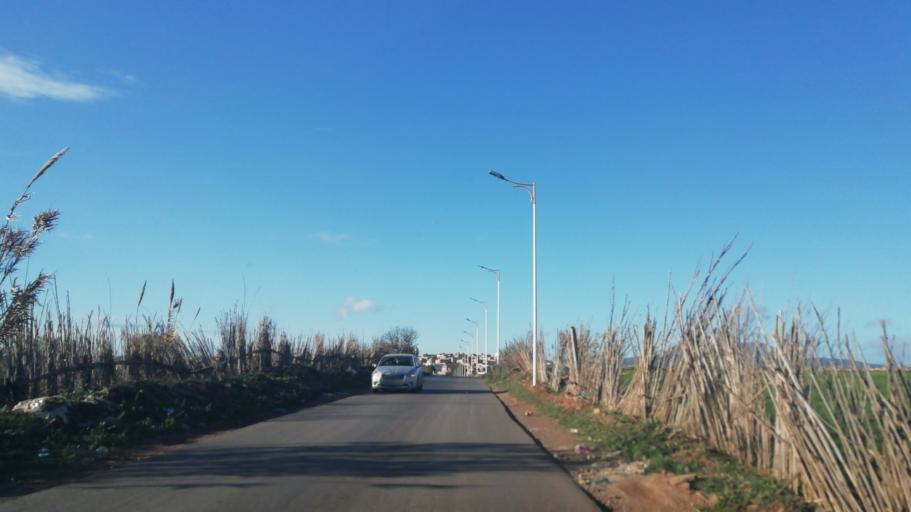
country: DZ
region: Oran
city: Sidi ech Chahmi
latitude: 35.6832
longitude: -0.4933
